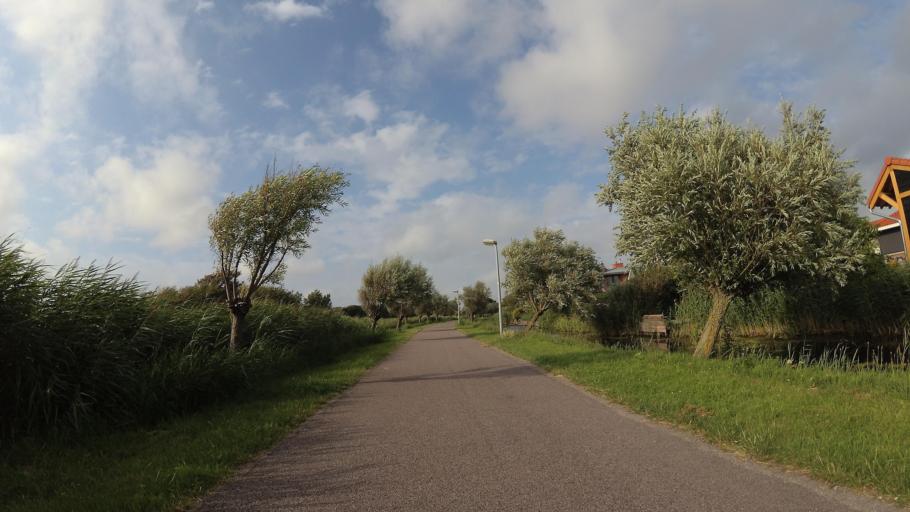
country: NL
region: North Holland
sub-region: Gemeente Den Helder
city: Den Helder
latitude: 52.8842
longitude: 4.7286
